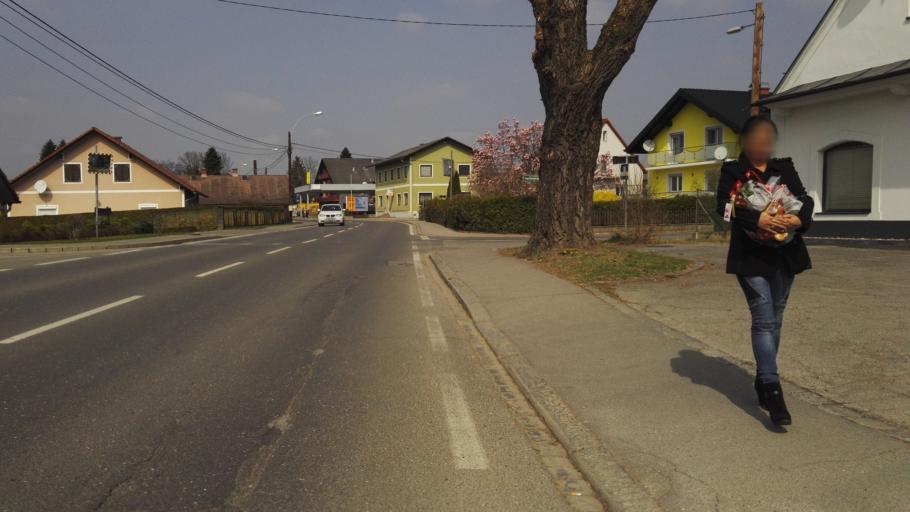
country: AT
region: Styria
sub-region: Politischer Bezirk Graz-Umgebung
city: Feldkirchen bei Graz
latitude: 47.0236
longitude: 15.4689
